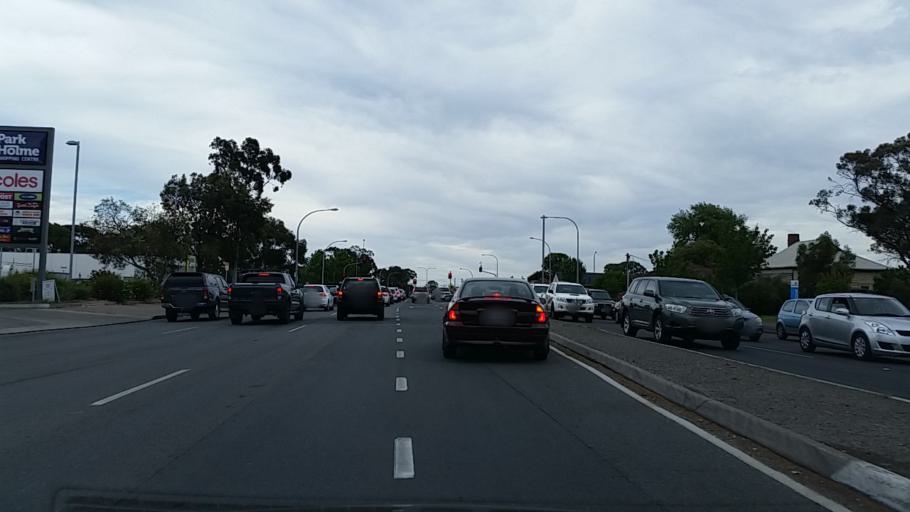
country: AU
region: South Australia
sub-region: Marion
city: Clovelly Park
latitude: -34.9950
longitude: 138.5571
